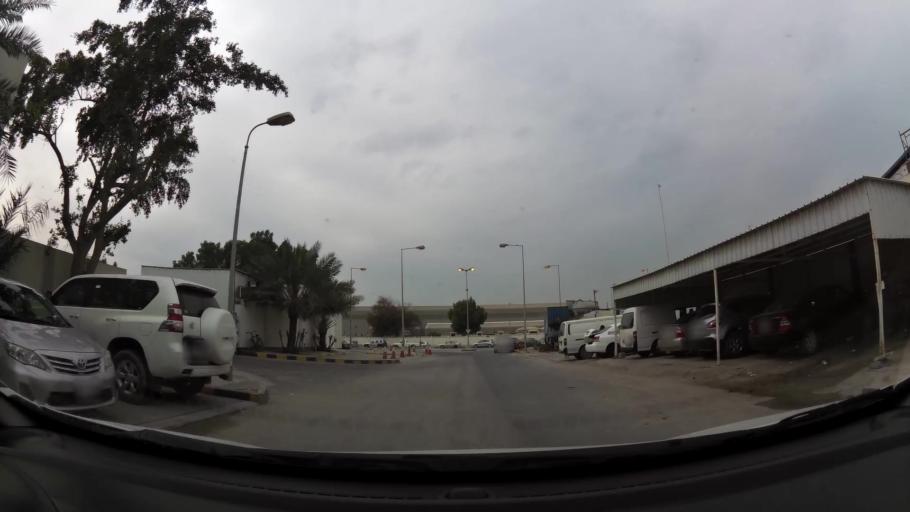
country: BH
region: Northern
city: Sitrah
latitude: 26.1786
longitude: 50.6162
